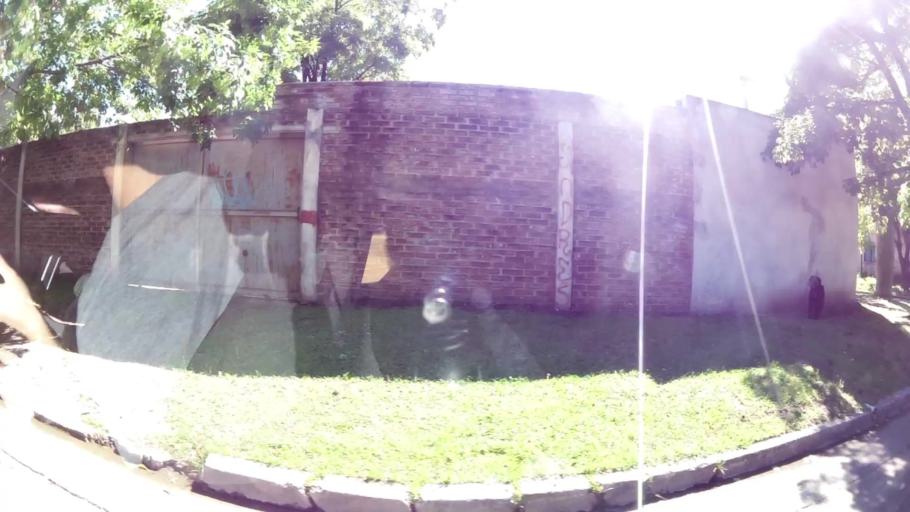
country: AR
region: Buenos Aires
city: Ituzaingo
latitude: -34.6272
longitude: -58.6541
